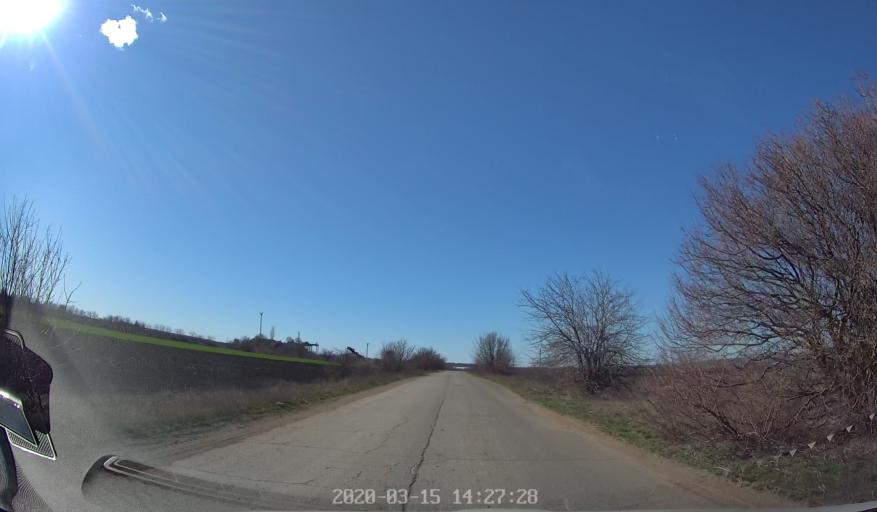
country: MD
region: Orhei
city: Orhei
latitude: 47.3451
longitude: 28.8941
